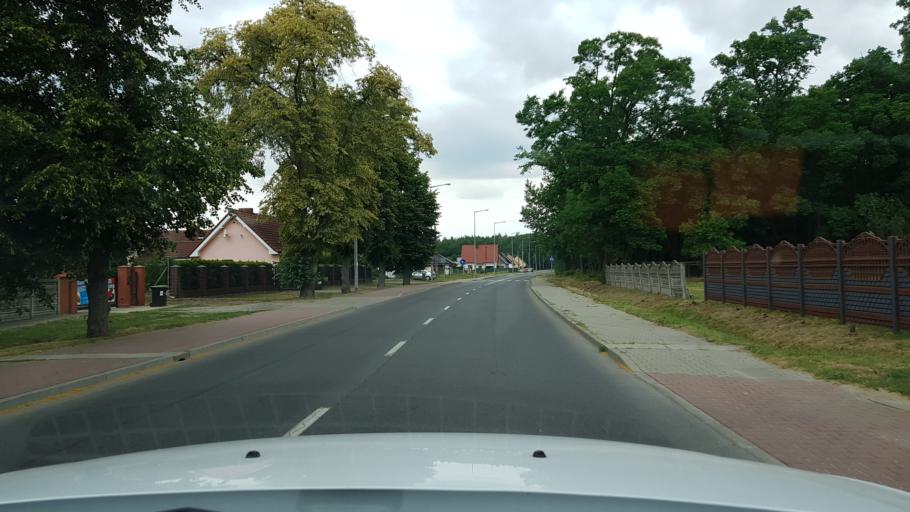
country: PL
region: Lubusz
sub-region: Powiat gorzowski
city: Kostrzyn nad Odra
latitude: 52.6151
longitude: 14.6168
